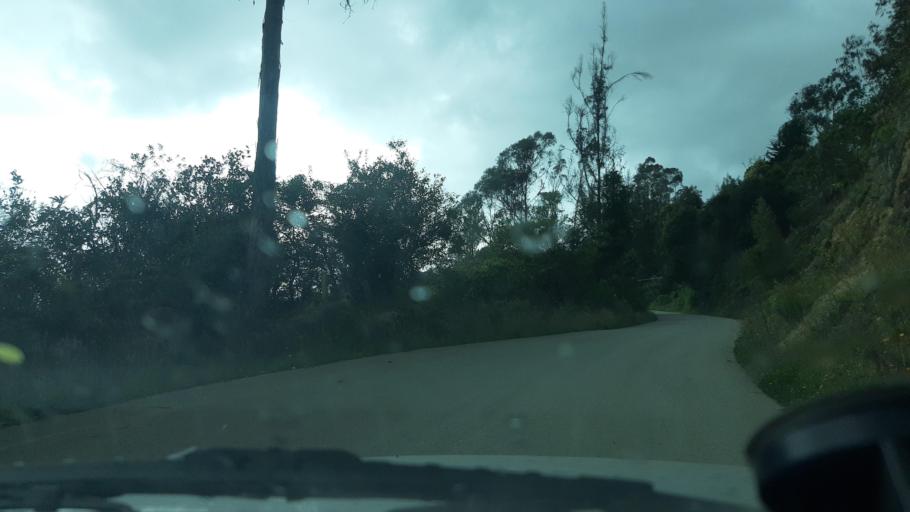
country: CO
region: Cundinamarca
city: Umbita
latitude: 5.2183
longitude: -73.4722
